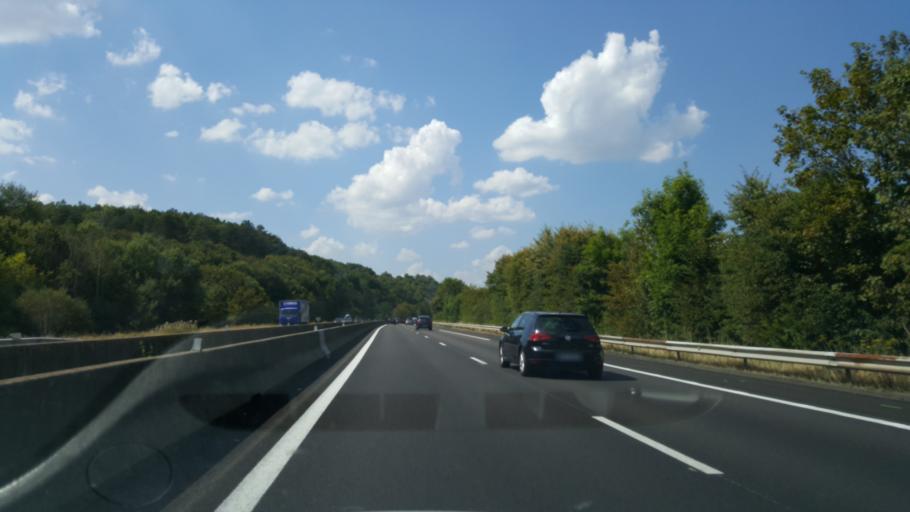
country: FR
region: Bourgogne
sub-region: Departement de la Cote-d'Or
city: Pouilly-en-Auxois
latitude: 47.1759
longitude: 4.6871
